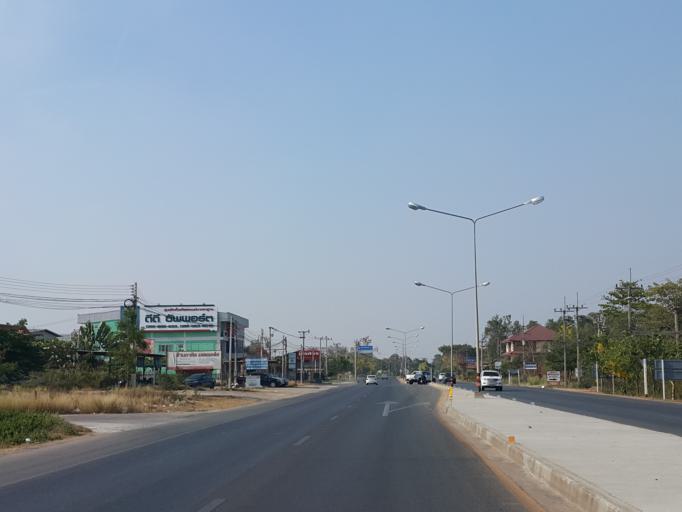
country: TH
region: Phitsanulok
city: Phitsanulok
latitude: 16.8262
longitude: 100.3320
